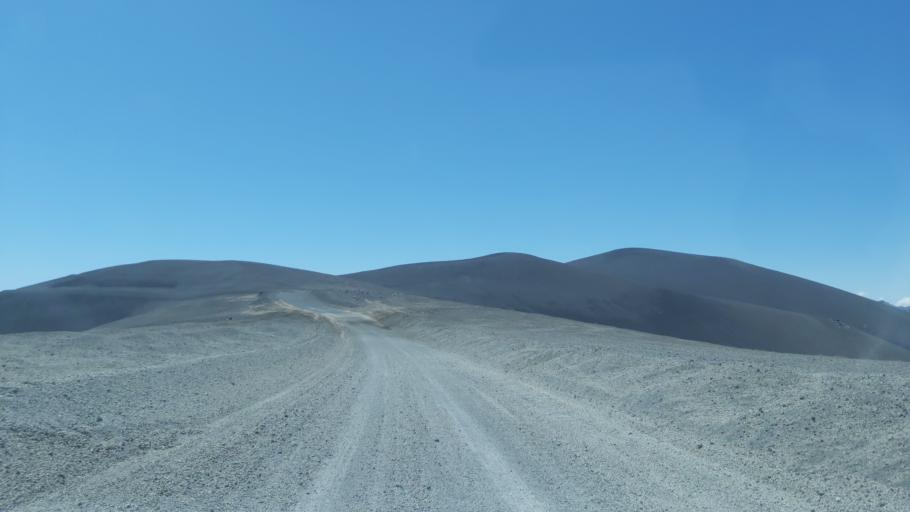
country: CL
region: Araucania
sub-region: Provincia de Cautin
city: Vilcun
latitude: -38.3763
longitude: -71.5407
